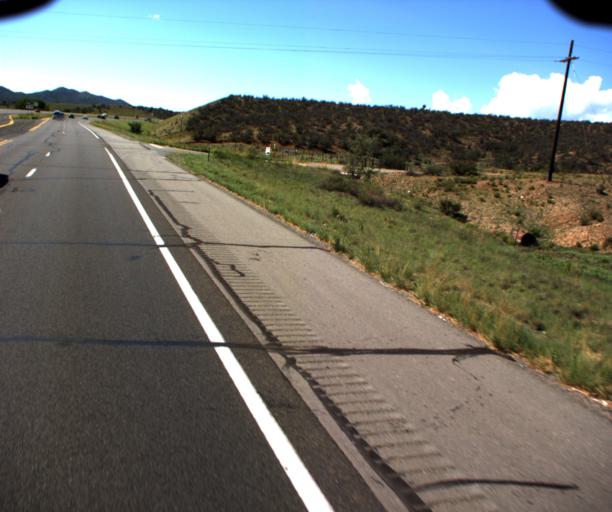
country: US
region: Arizona
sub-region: Yavapai County
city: Dewey-Humboldt
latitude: 34.5221
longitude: -112.2391
